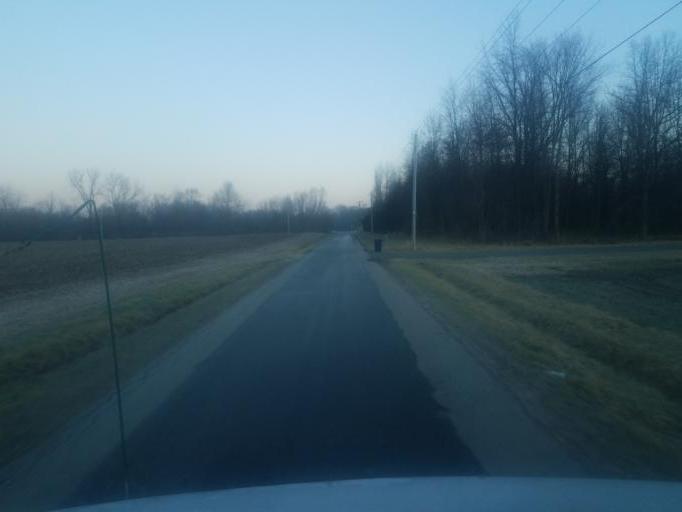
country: US
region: Ohio
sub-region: Crawford County
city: Galion
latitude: 40.7429
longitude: -82.8724
